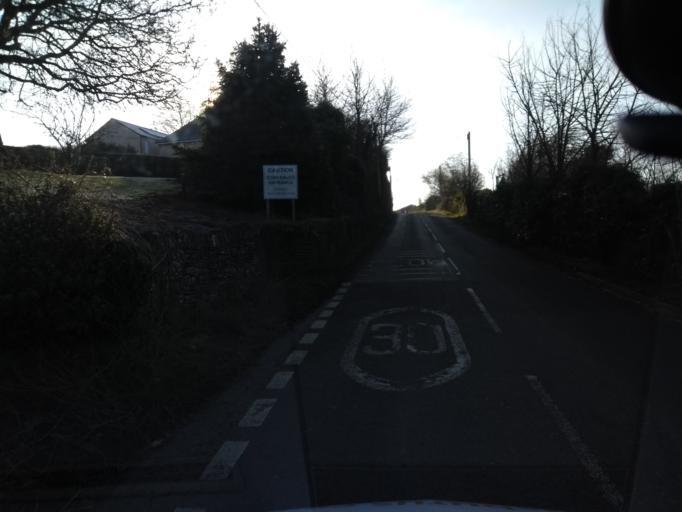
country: GB
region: England
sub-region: Somerset
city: Bruton
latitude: 51.1103
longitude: -2.4498
